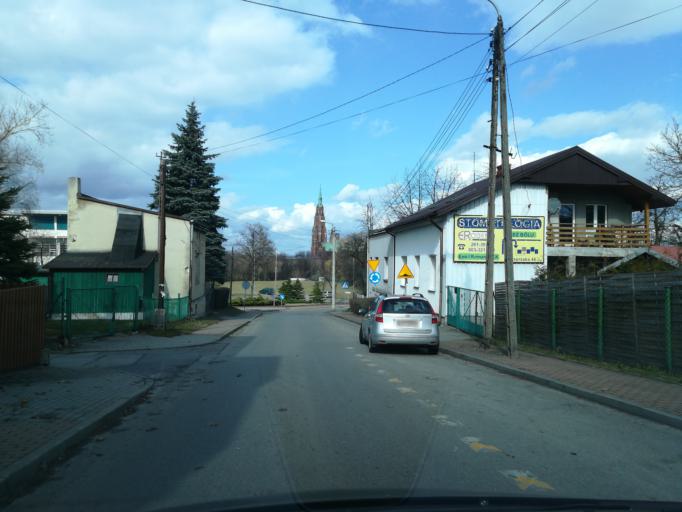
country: PL
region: Silesian Voivodeship
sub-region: Dabrowa Gornicza
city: Dabrowa Gornicza
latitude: 50.3191
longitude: 19.1912
